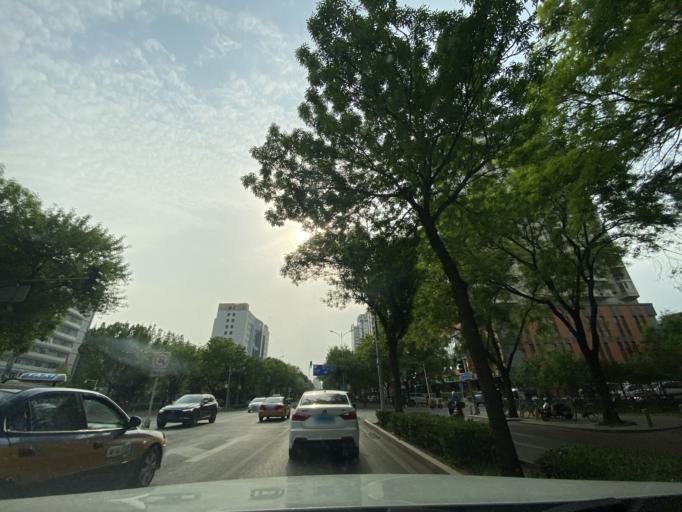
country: CN
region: Beijing
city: Qinghe
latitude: 39.9752
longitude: 116.3424
